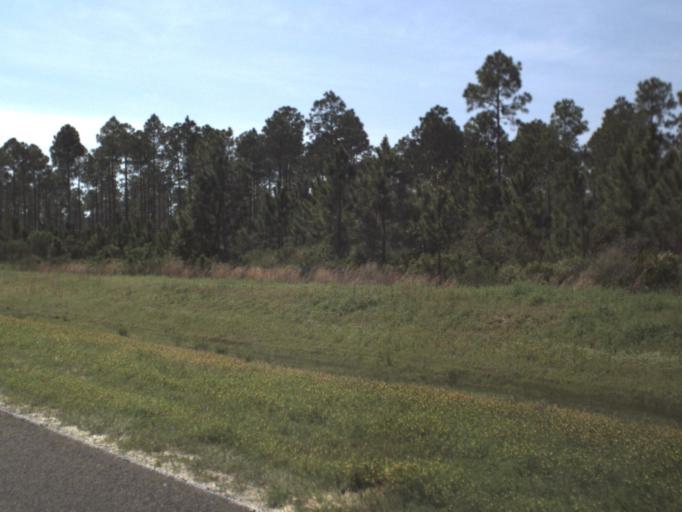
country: US
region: Florida
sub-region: Bay County
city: Laguna Beach
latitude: 30.2494
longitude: -85.8796
